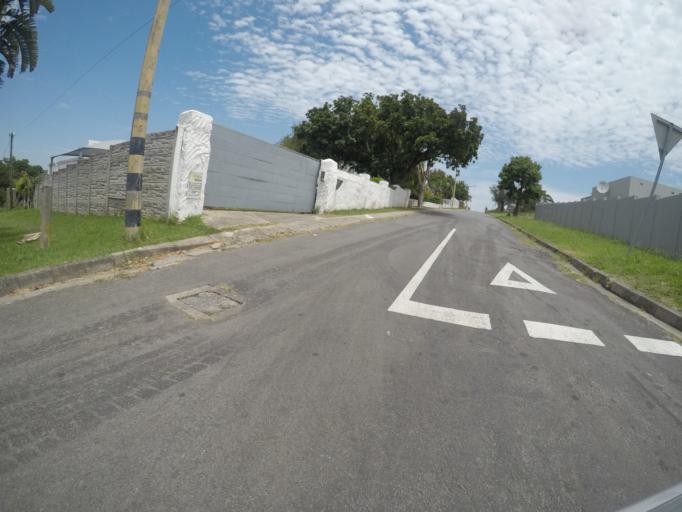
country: ZA
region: Eastern Cape
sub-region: Buffalo City Metropolitan Municipality
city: East London
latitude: -32.9829
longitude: 27.8671
